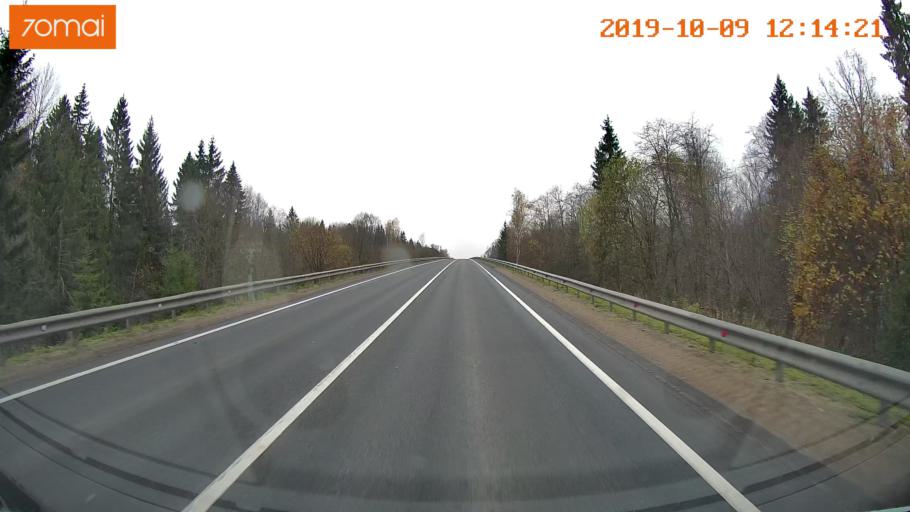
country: RU
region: Jaroslavl
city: Prechistoye
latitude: 58.4973
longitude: 40.3379
